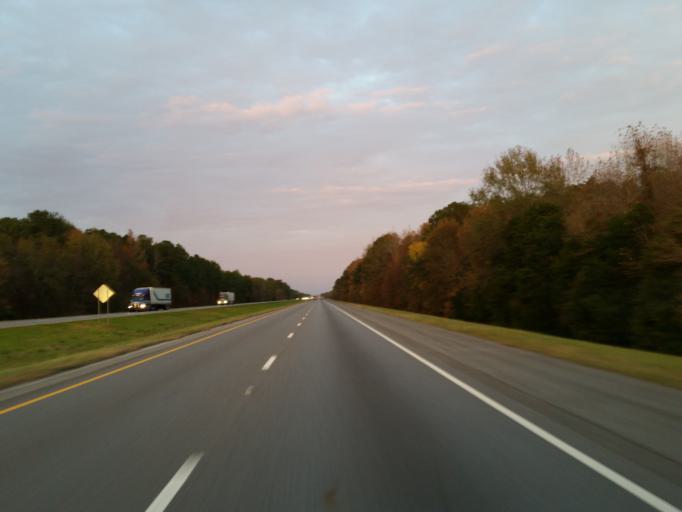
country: US
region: Alabama
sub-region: Sumter County
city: Livingston
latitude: 32.7185
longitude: -88.1223
